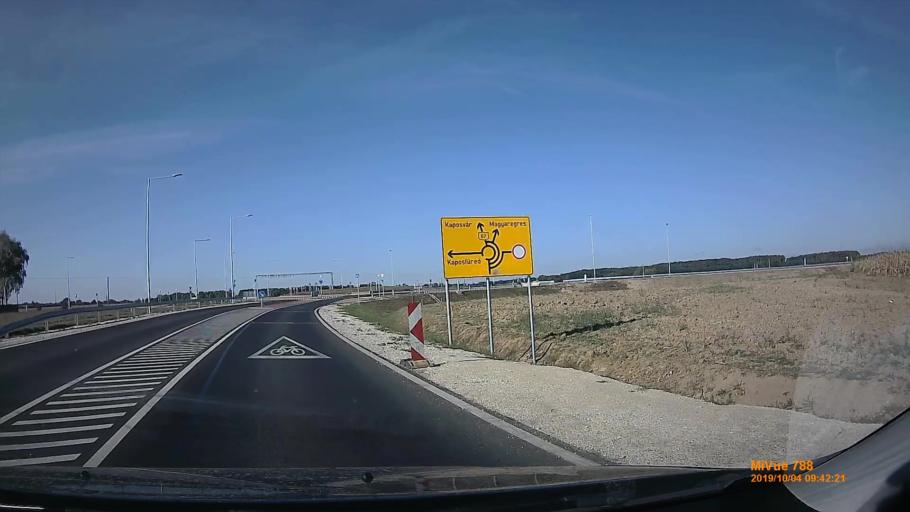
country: HU
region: Somogy
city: Kaposvar
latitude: 46.4250
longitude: 17.7761
